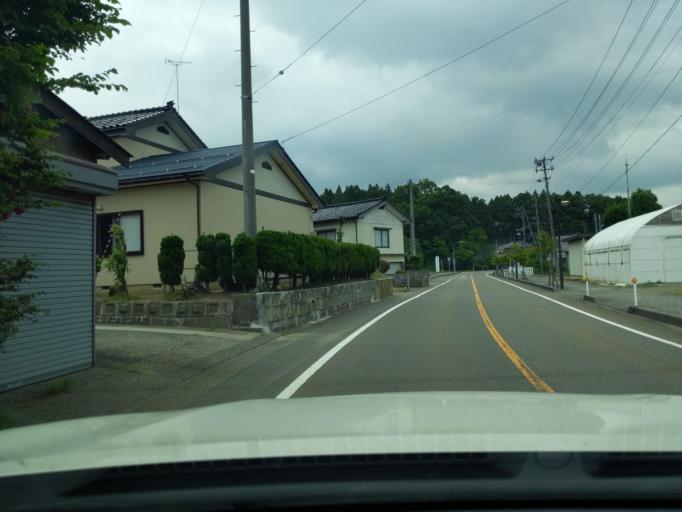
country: JP
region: Niigata
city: Kashiwazaki
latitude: 37.3380
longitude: 138.5742
